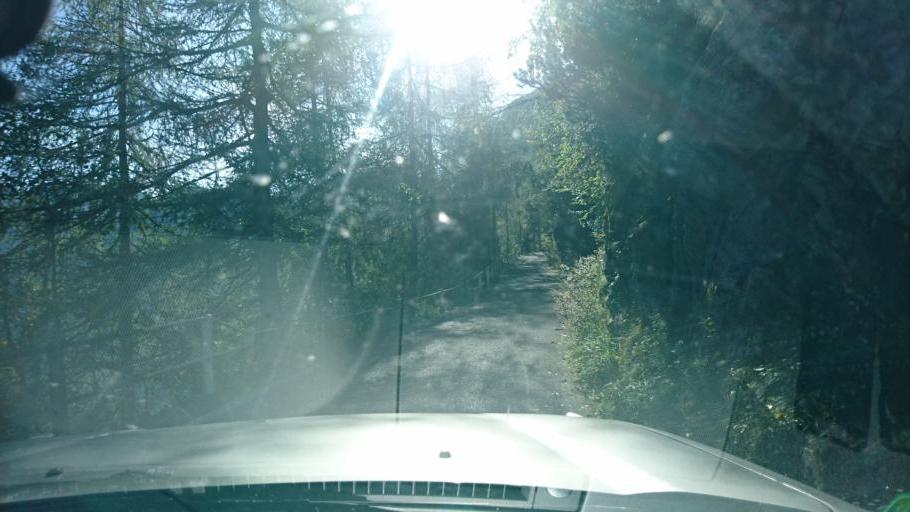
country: IT
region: Lombardy
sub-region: Provincia di Brescia
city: Lozio
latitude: 46.0459
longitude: 10.2216
